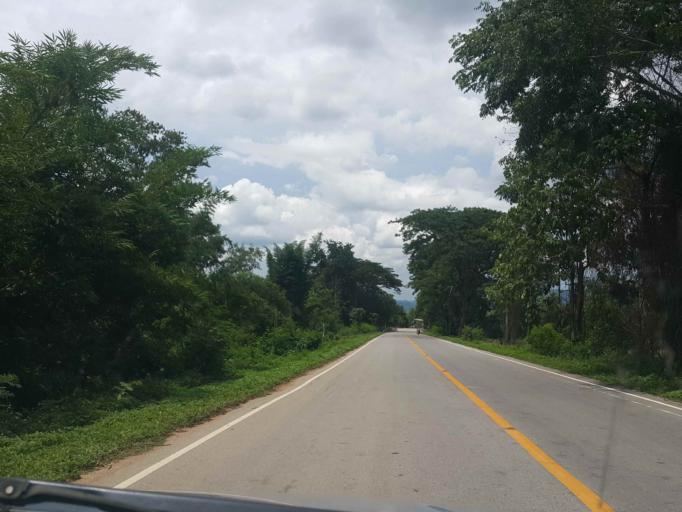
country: TH
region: Nan
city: Ban Luang
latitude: 18.8460
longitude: 100.4214
